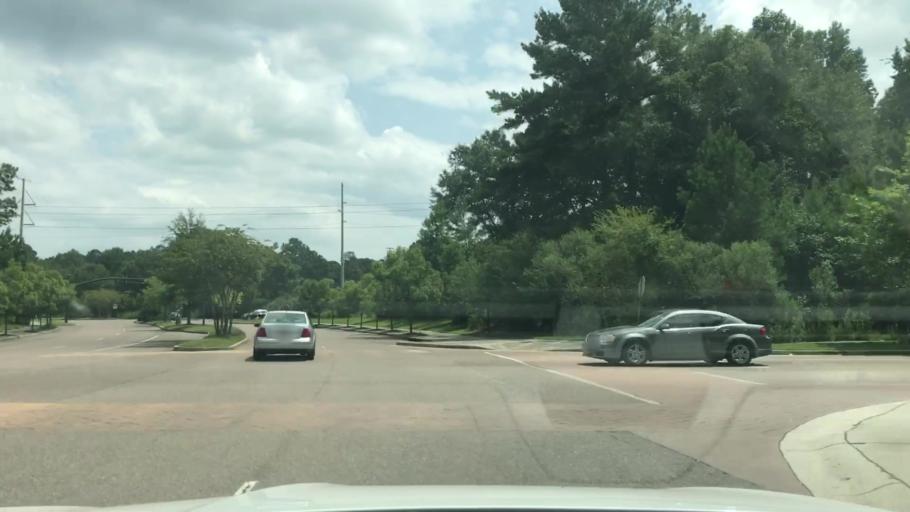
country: US
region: South Carolina
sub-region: Charleston County
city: Shell Point
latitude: 32.8244
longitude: -80.0822
